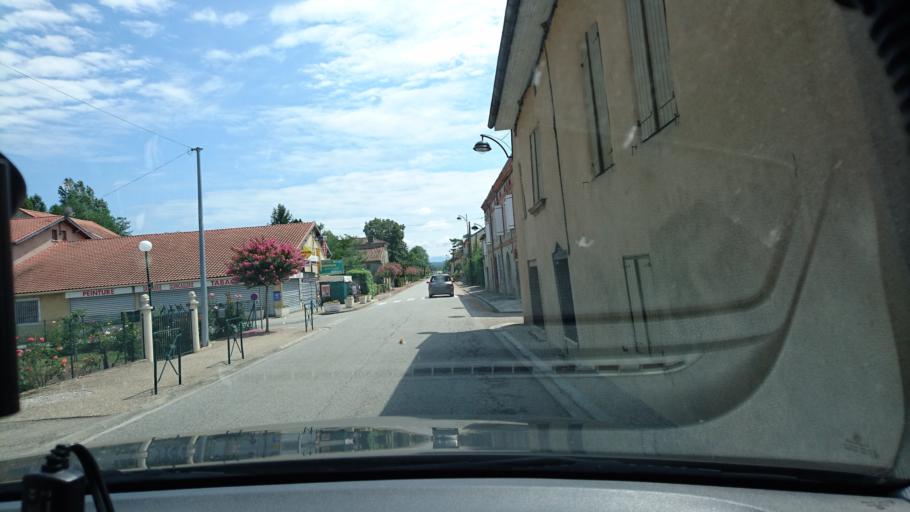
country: FR
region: Midi-Pyrenees
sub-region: Departement de la Haute-Garonne
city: Gaillac-Toulza
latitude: 43.1736
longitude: 1.4087
